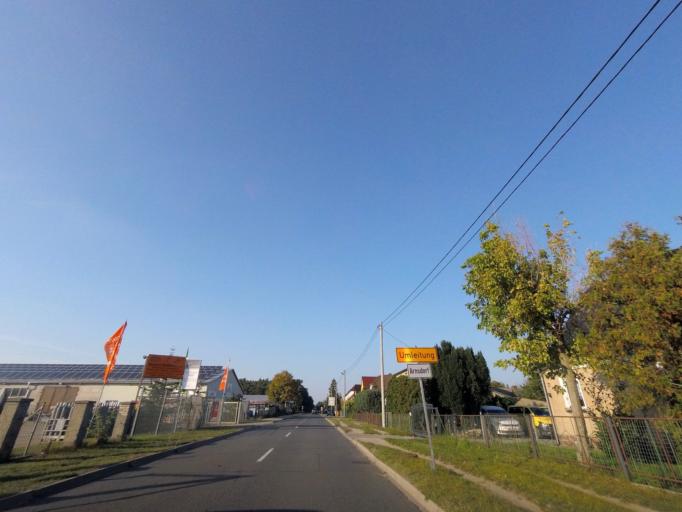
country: DE
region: Saxony-Anhalt
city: Jessen
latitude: 51.7984
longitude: 12.9544
